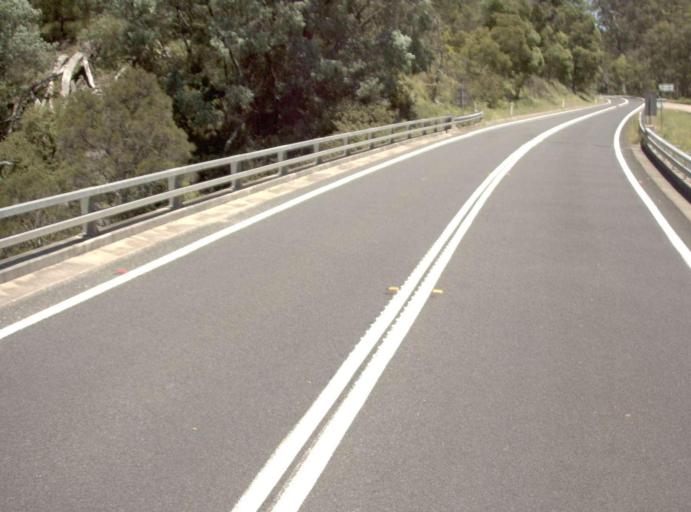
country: AU
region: Victoria
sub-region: East Gippsland
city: Lakes Entrance
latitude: -37.8023
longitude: 148.0469
